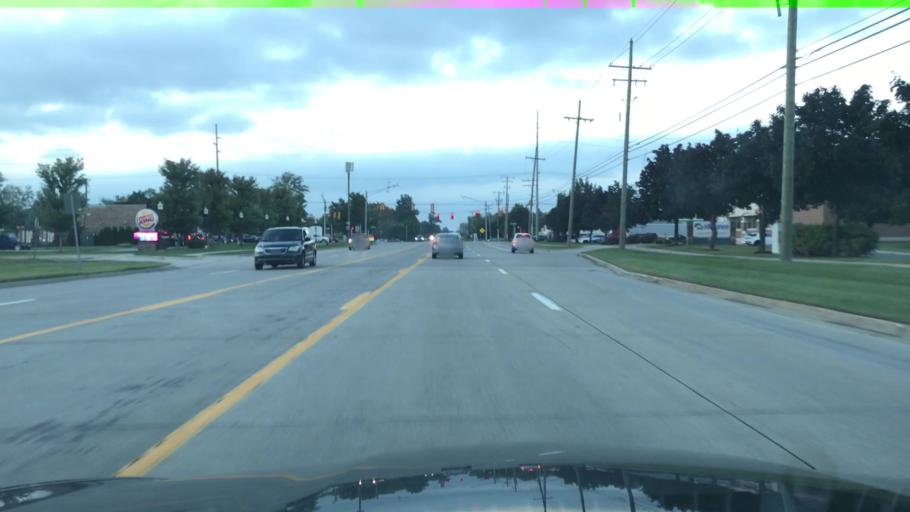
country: US
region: Michigan
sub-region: Macomb County
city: Shelby
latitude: 42.6687
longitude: -82.9946
